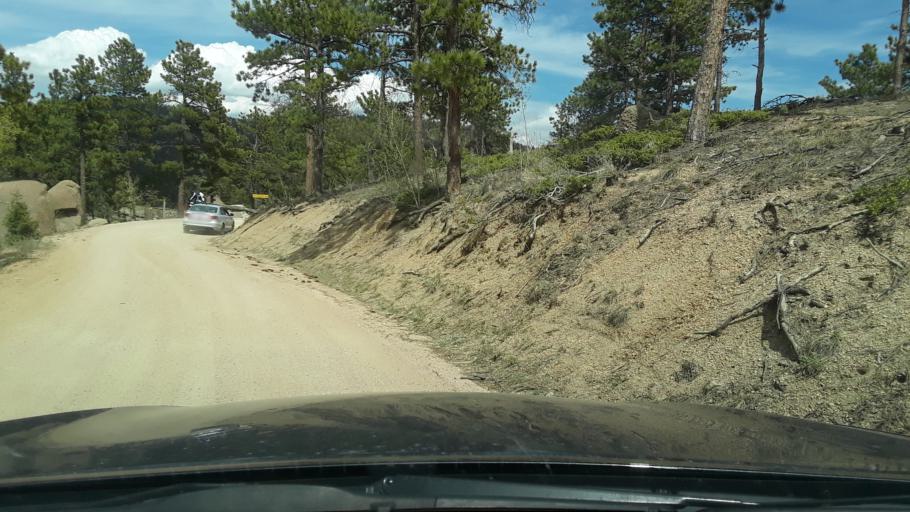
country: US
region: Colorado
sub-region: El Paso County
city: Palmer Lake
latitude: 39.0711
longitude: -104.9432
